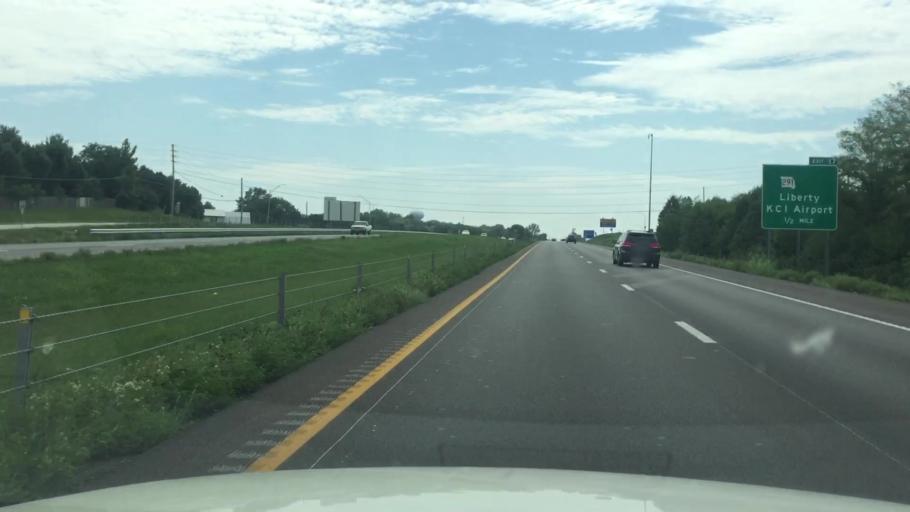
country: US
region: Missouri
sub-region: Clay County
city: Liberty
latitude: 39.2713
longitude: -94.4343
